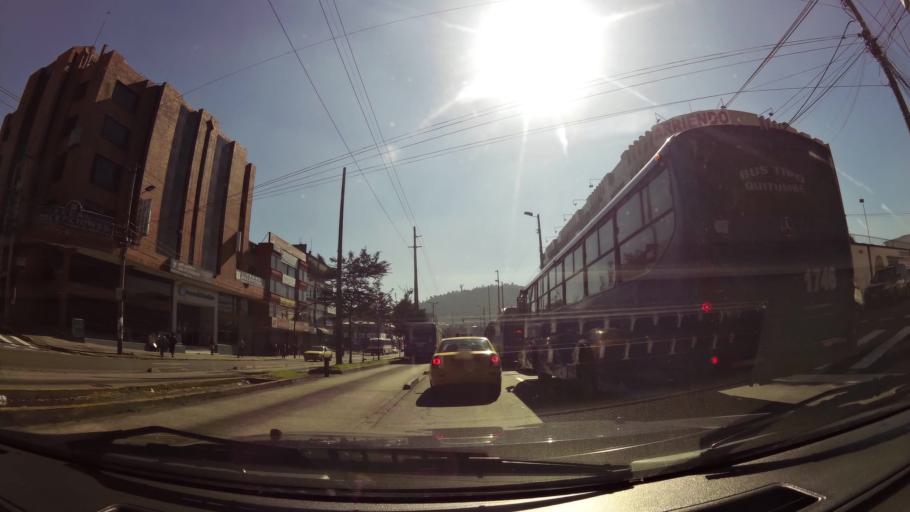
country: EC
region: Pichincha
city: Quito
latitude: -0.2384
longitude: -78.5295
